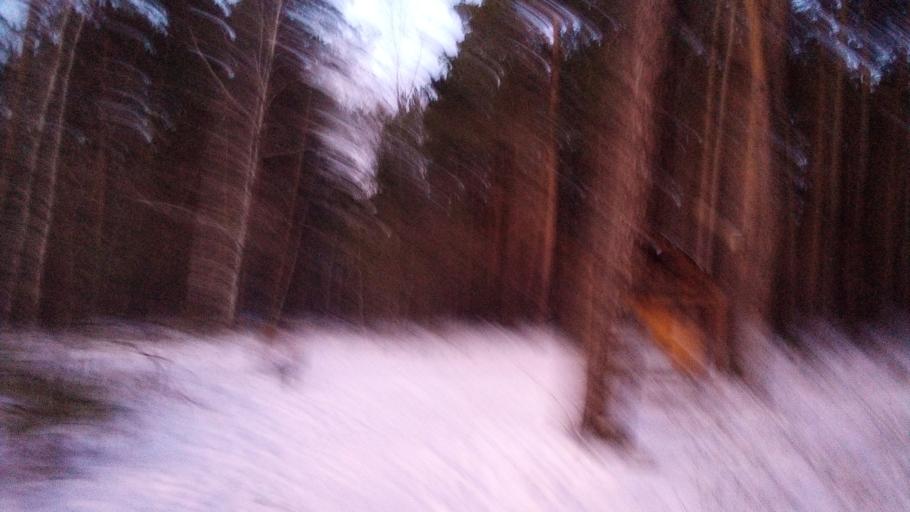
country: RU
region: Chelyabinsk
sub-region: Gorod Chelyabinsk
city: Chelyabinsk
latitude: 55.1653
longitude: 61.3316
